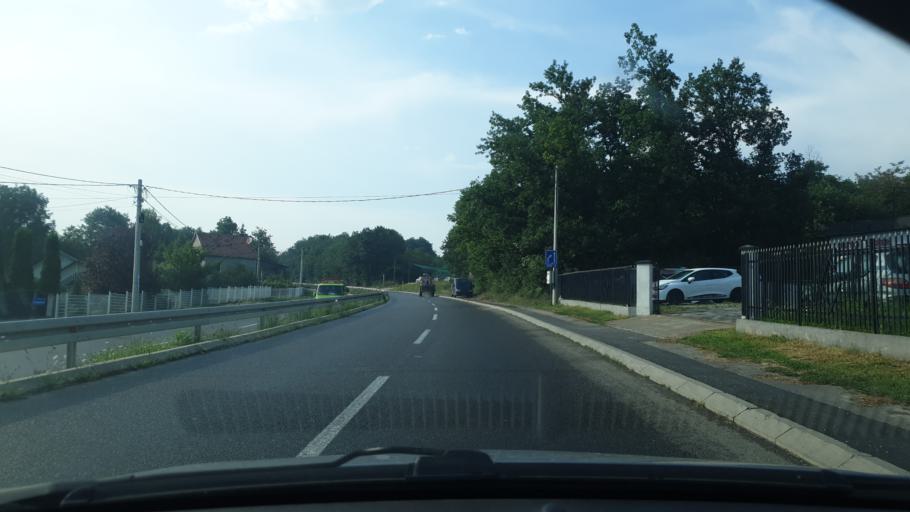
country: RS
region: Central Serbia
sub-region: Sumadijski Okrug
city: Kragujevac
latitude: 44.0550
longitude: 20.8969
